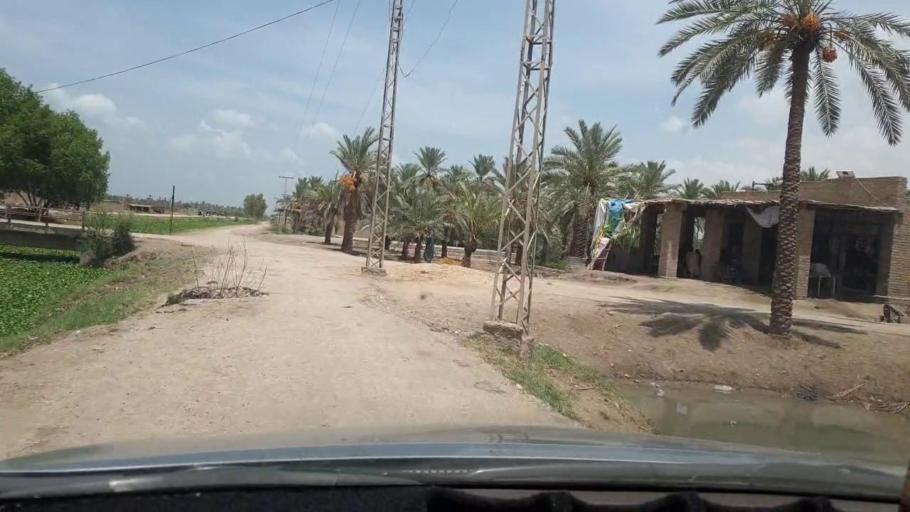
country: PK
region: Sindh
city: Khairpur
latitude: 27.4501
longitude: 68.7869
